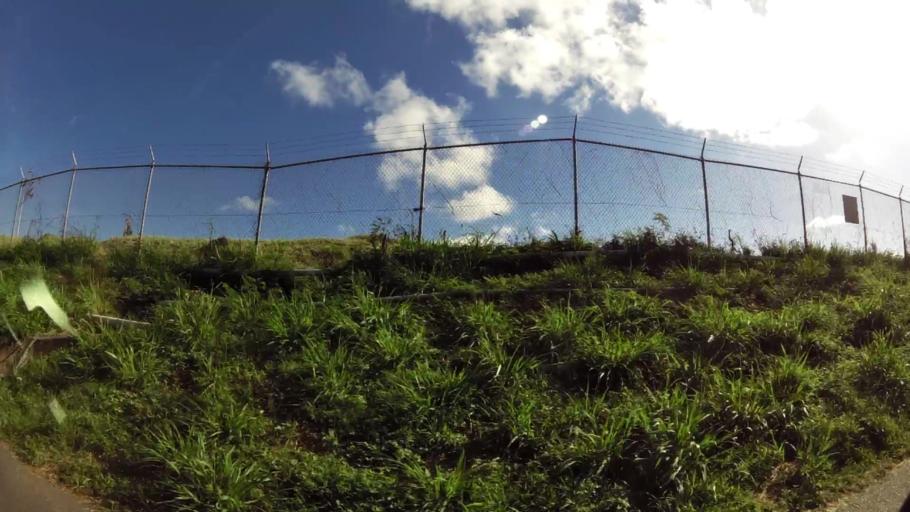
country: TT
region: Tobago
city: Scarborough
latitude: 11.1508
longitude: -60.8452
